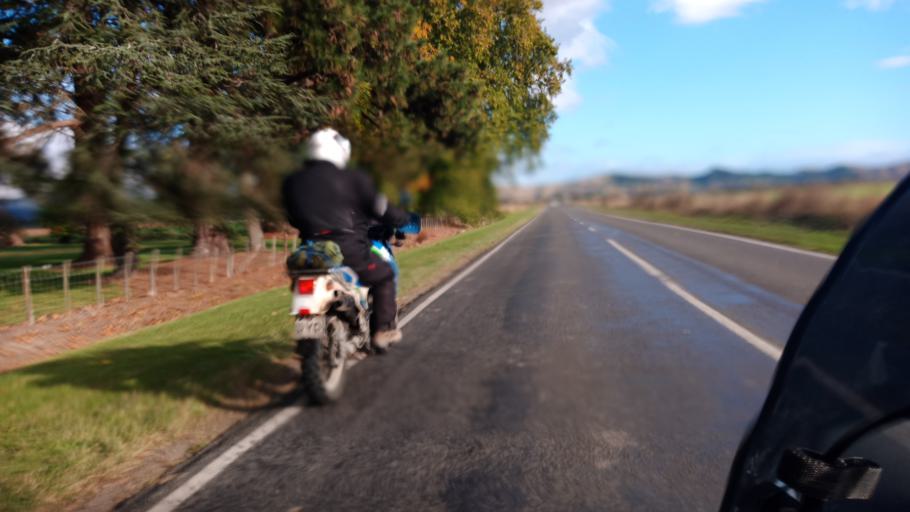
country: NZ
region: Gisborne
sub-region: Gisborne District
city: Gisborne
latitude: -38.6364
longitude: 177.9096
